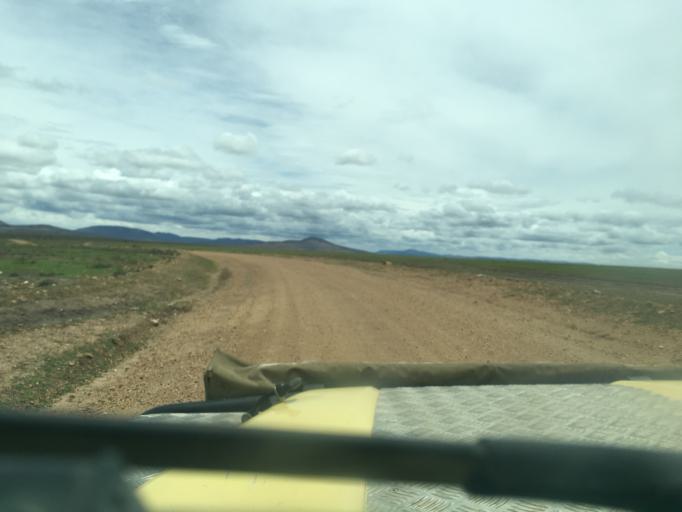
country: KE
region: Kajiado
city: Magadi
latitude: -2.0938
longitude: 35.5442
